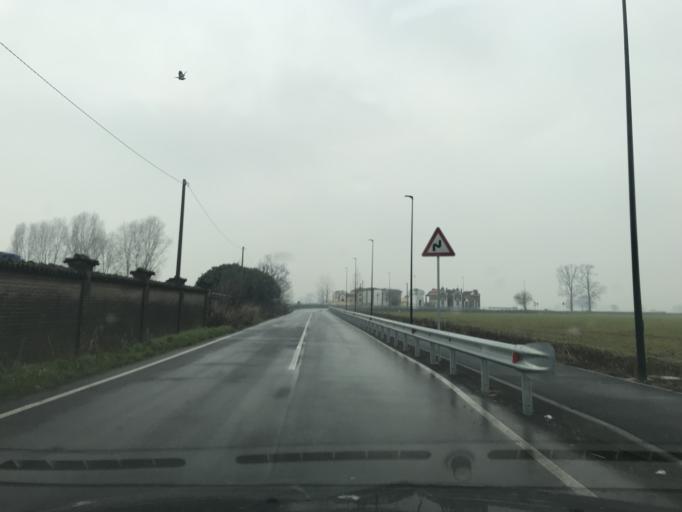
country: IT
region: Lombardy
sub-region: Provincia di Lodi
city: Villanova del Sillaro
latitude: 45.2385
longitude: 9.4792
